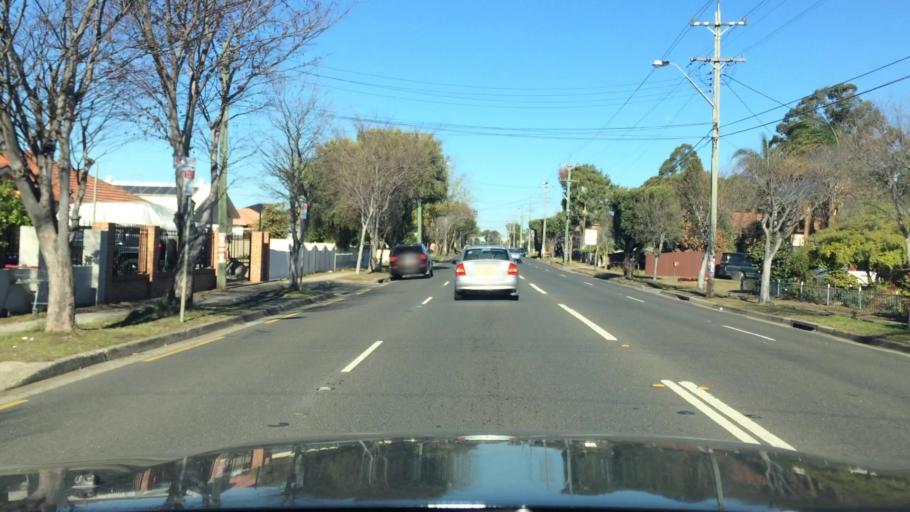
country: AU
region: New South Wales
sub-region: Fairfield
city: Fairfield Heights
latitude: -33.8580
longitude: 150.9511
